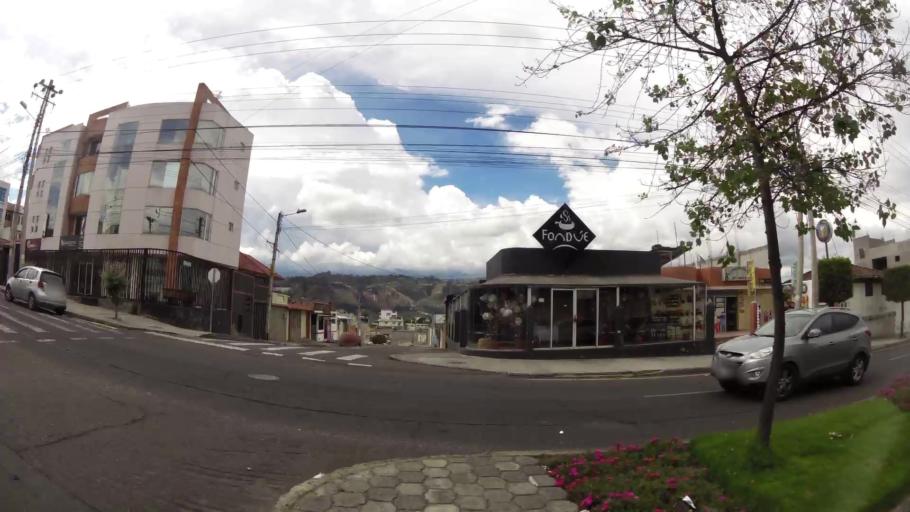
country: EC
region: Tungurahua
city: Ambato
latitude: -1.2672
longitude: -78.6323
